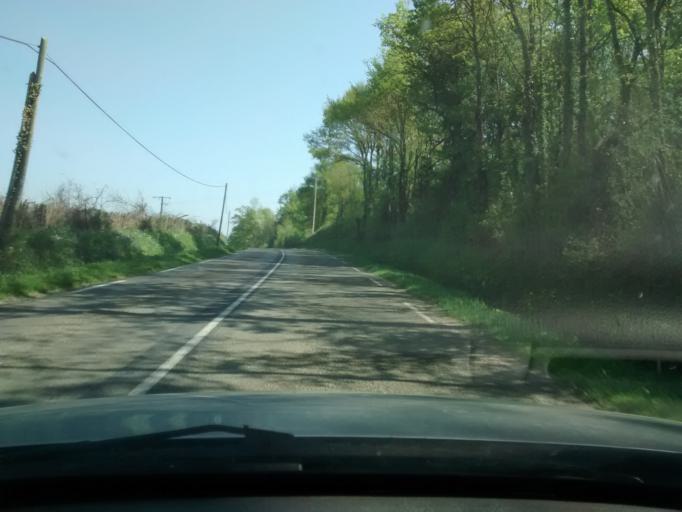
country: FR
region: Pays de la Loire
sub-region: Departement de la Mayenne
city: Soulge-sur-Ouette
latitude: 48.0944
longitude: -0.5250
